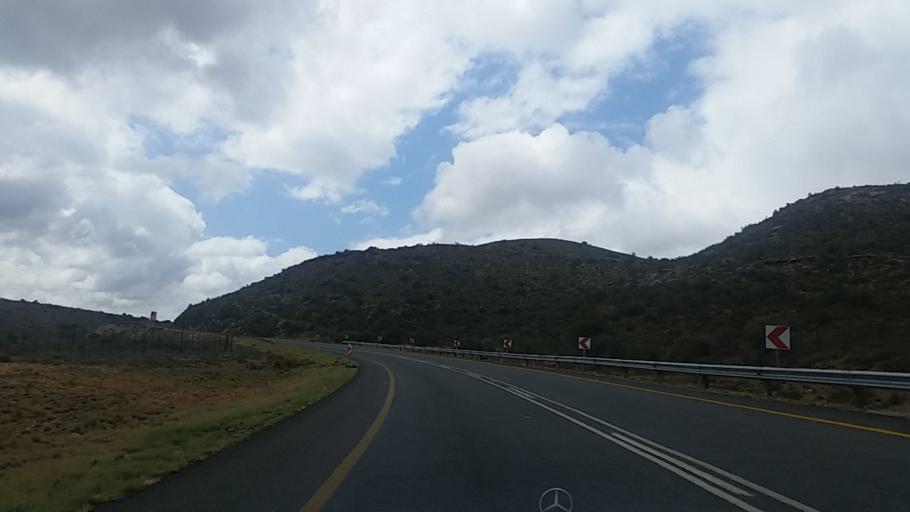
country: ZA
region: Eastern Cape
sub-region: Cacadu District Municipality
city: Graaff-Reinet
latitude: -32.1177
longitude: 24.6082
